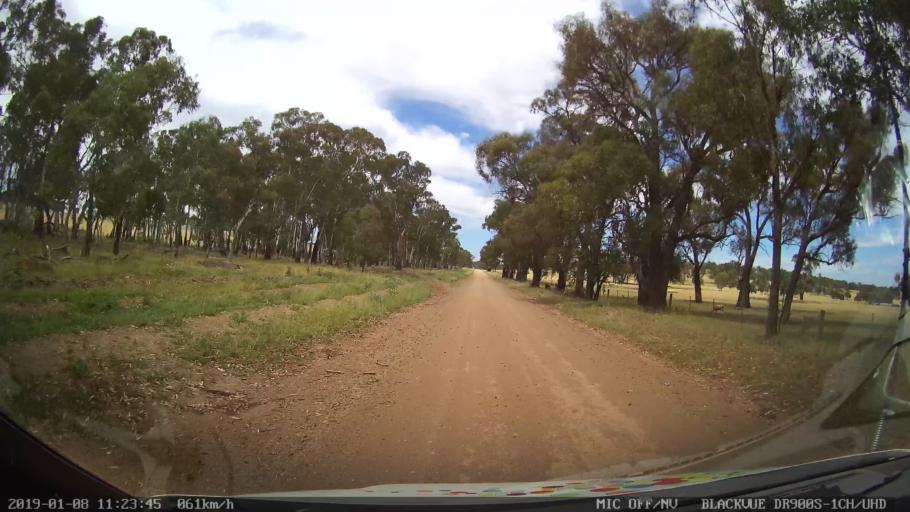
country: AU
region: New South Wales
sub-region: Guyra
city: Guyra
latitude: -30.2582
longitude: 151.5586
